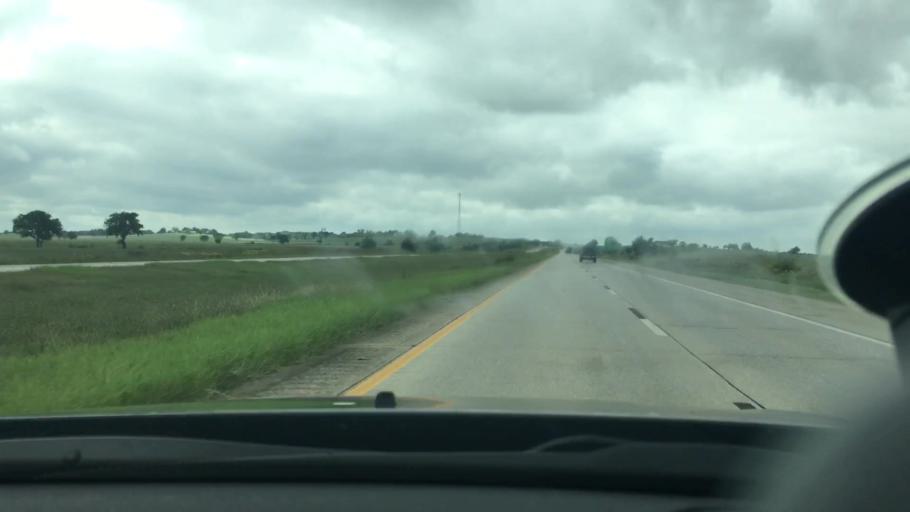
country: US
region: Oklahoma
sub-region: Bryan County
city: Durant
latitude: 34.1520
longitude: -96.2623
